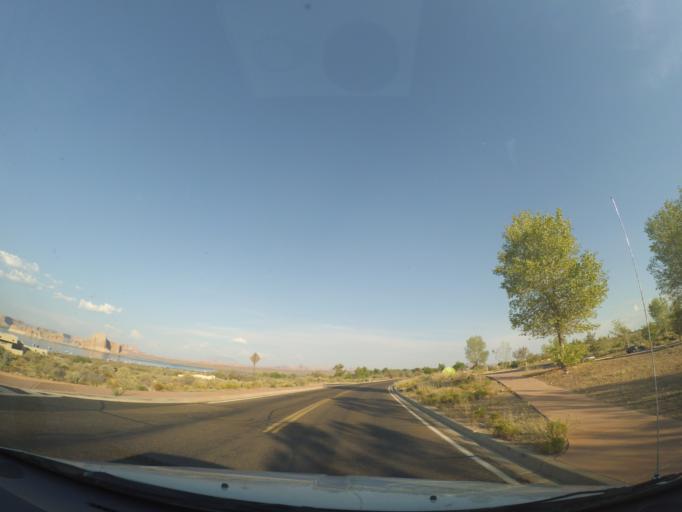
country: US
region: Arizona
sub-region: Coconino County
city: Page
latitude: 36.9990
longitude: -111.4977
